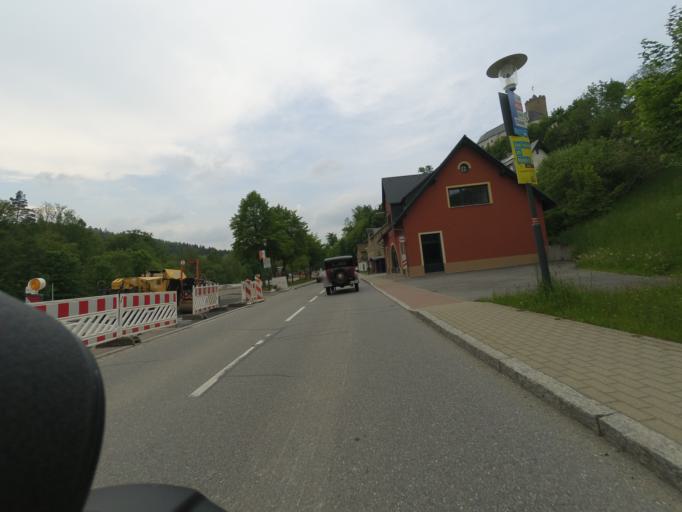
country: DE
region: Saxony
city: Scharfenstein
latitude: 50.7033
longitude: 13.0559
